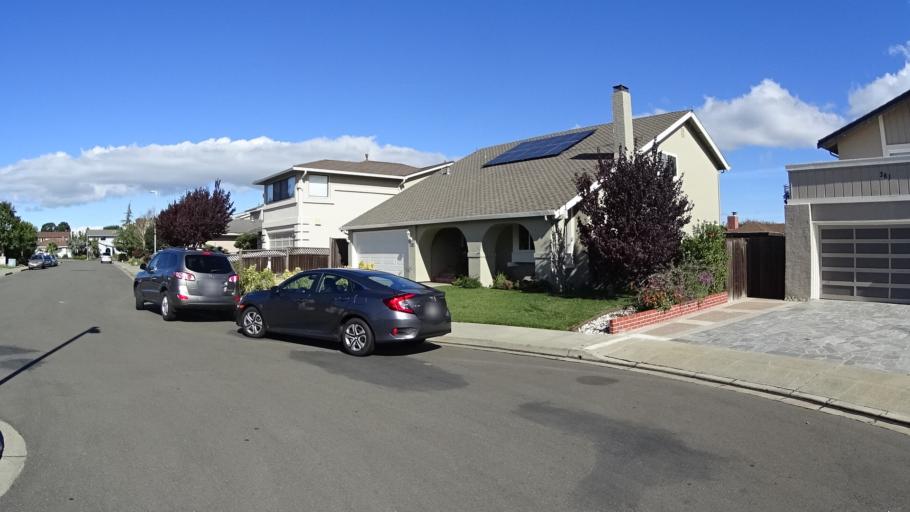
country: US
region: California
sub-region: San Mateo County
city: Foster City
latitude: 37.5567
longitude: -122.2516
